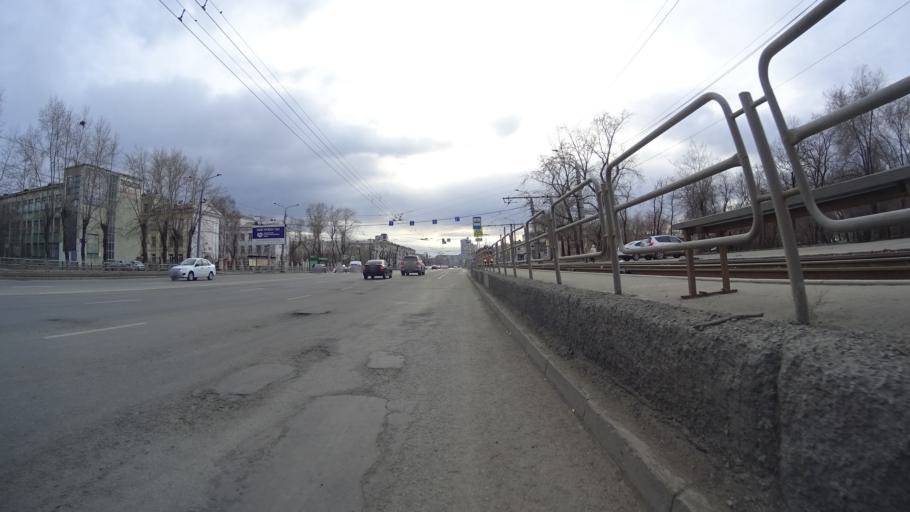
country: RU
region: Chelyabinsk
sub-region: Gorod Chelyabinsk
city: Chelyabinsk
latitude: 55.1601
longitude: 61.4532
